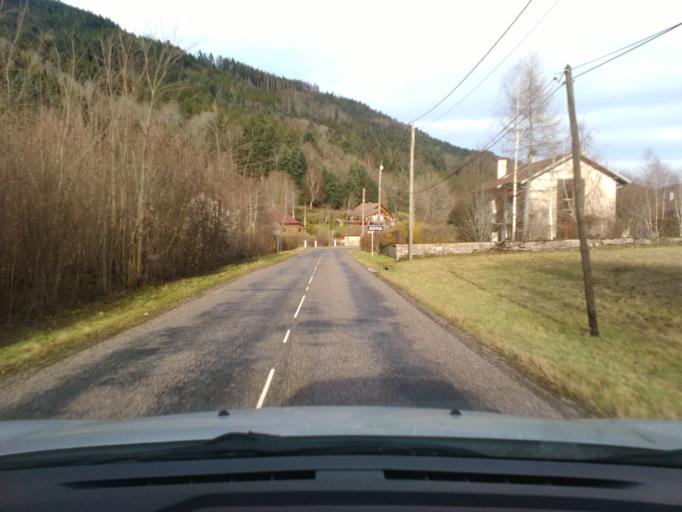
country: FR
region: Lorraine
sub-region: Departement des Vosges
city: Anould
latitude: 48.1338
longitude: 6.9571
